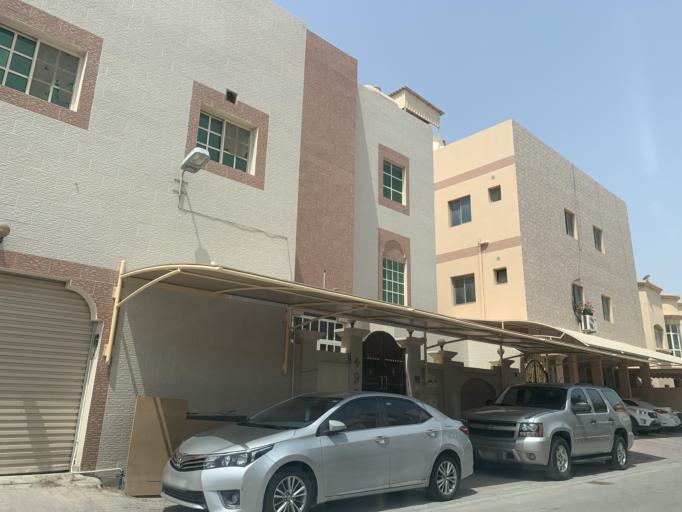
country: BH
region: Northern
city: Madinat `Isa
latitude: 26.1834
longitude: 50.5521
